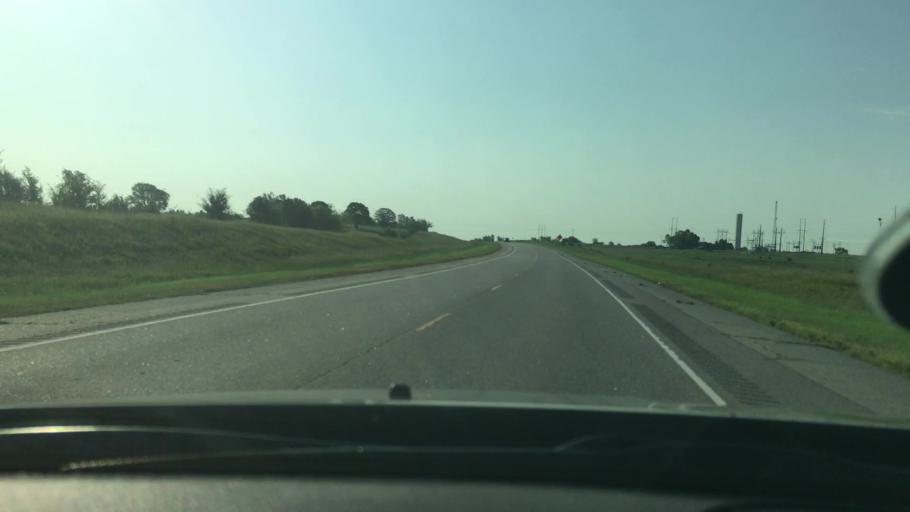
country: US
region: Oklahoma
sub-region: Coal County
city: Coalgate
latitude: 34.6167
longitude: -96.4465
